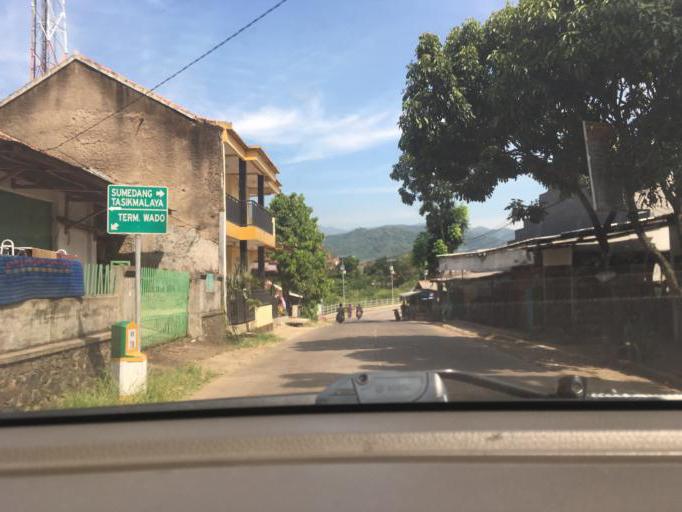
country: ID
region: West Java
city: Cilengkrang
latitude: -6.9458
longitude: 108.0951
